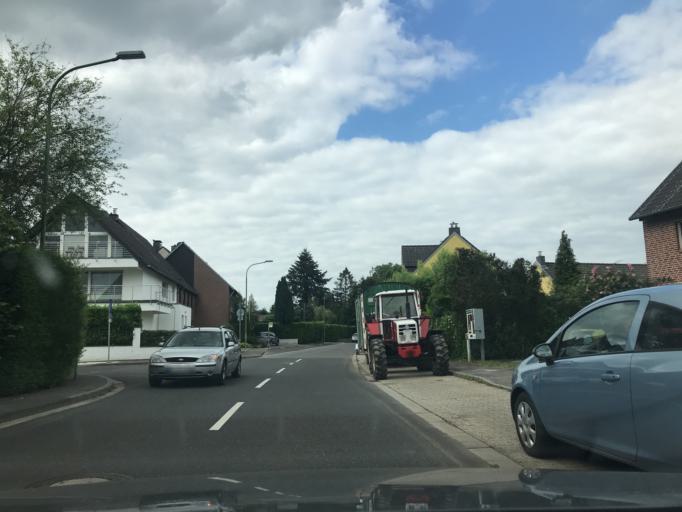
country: DE
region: North Rhine-Westphalia
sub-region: Regierungsbezirk Dusseldorf
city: Neuss
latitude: 51.1412
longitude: 6.7217
